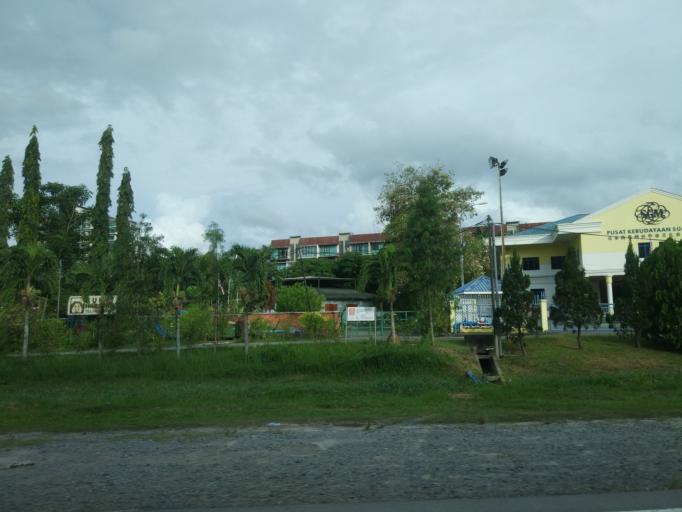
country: MY
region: Sabah
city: Kota Kinabalu
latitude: 6.0163
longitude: 116.1377
